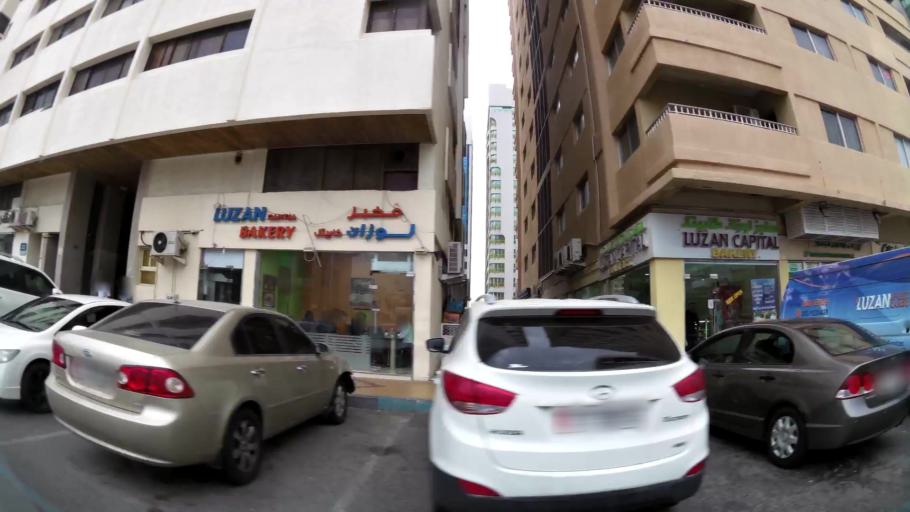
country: AE
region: Abu Dhabi
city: Abu Dhabi
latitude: 24.4812
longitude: 54.3718
